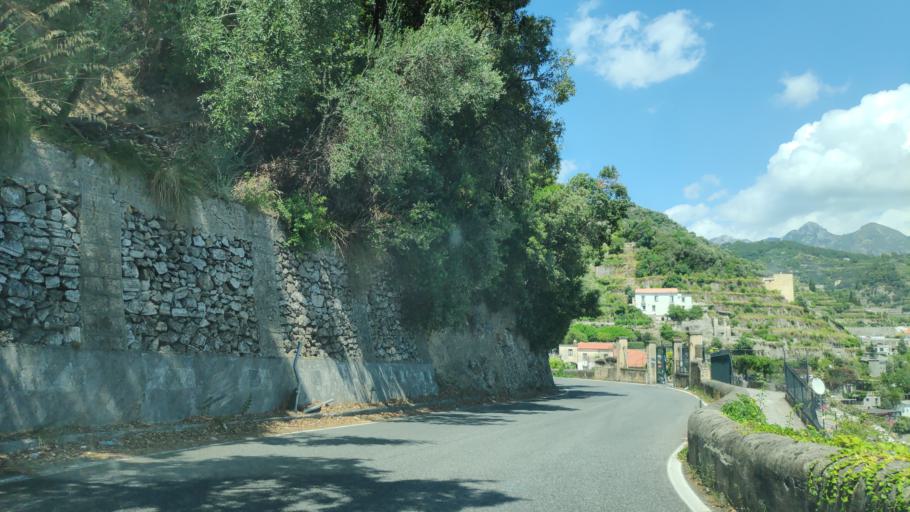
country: IT
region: Campania
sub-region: Provincia di Salerno
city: Ravello
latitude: 40.6448
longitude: 14.6185
